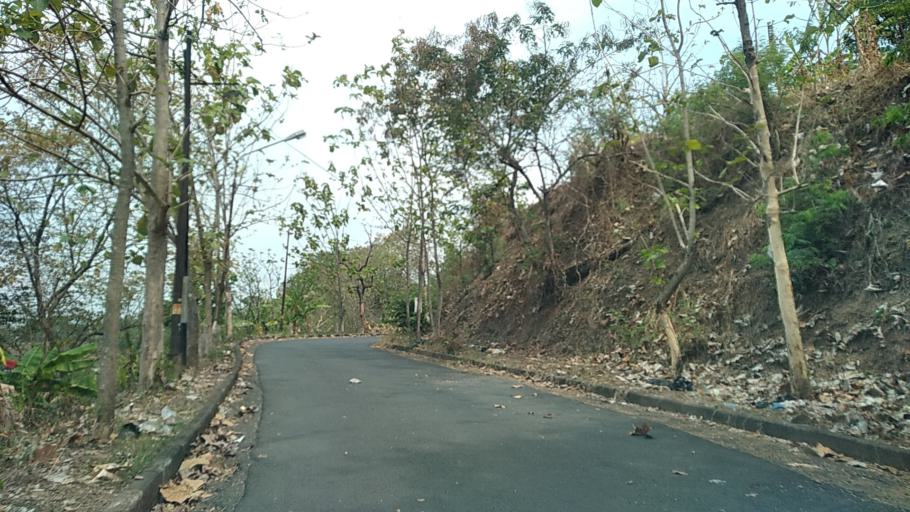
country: ID
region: Central Java
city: Semarang
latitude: -7.0449
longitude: 110.4410
